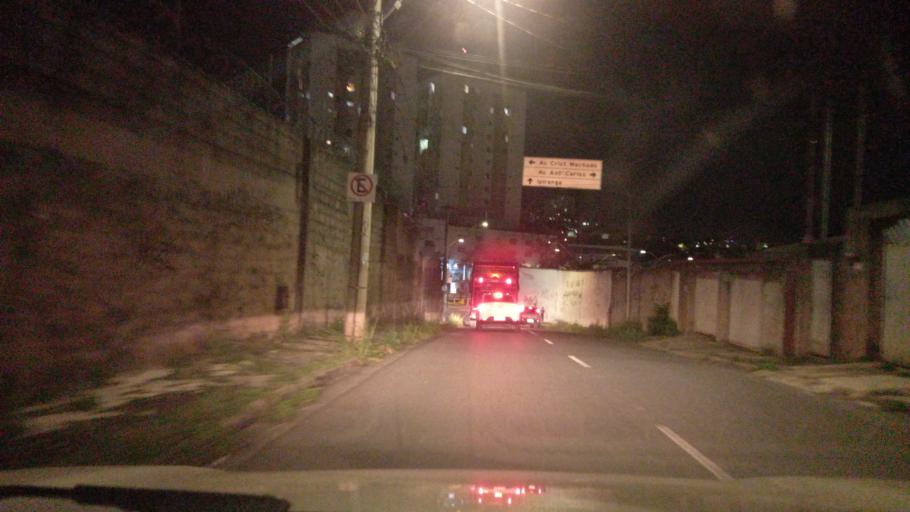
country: BR
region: Minas Gerais
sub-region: Belo Horizonte
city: Belo Horizonte
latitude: -19.8800
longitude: -43.9360
